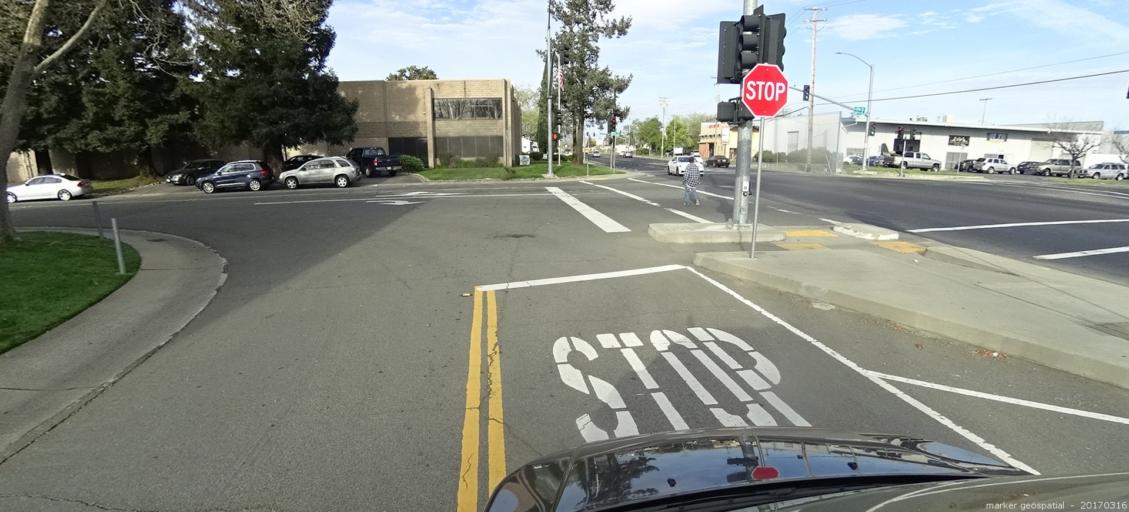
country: US
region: California
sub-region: Sacramento County
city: Parkway
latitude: 38.5101
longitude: -121.4767
